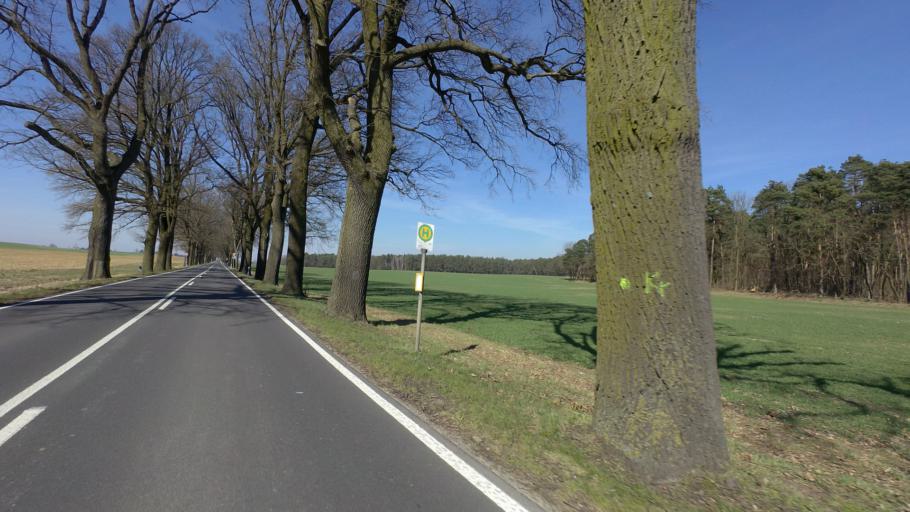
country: DE
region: Brandenburg
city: Waldsieversdorf
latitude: 52.5608
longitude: 14.0385
